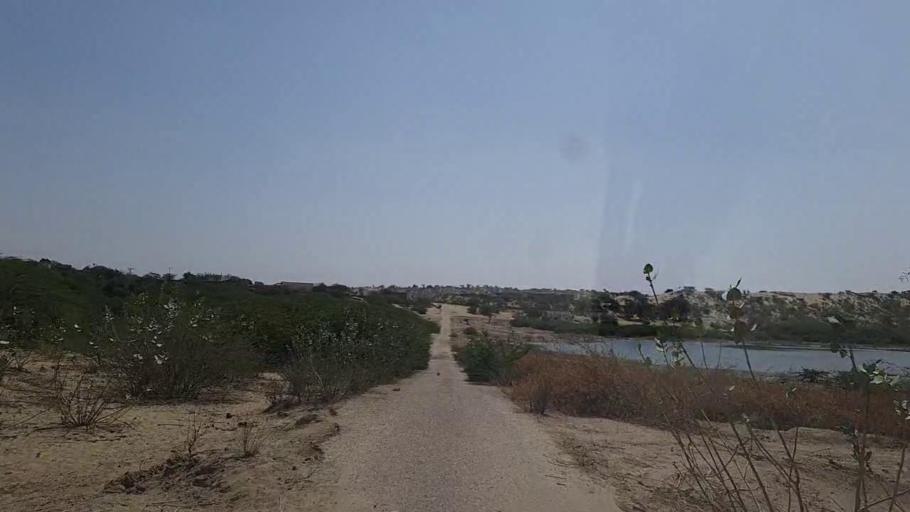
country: PK
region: Sindh
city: Diplo
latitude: 24.5129
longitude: 69.4137
